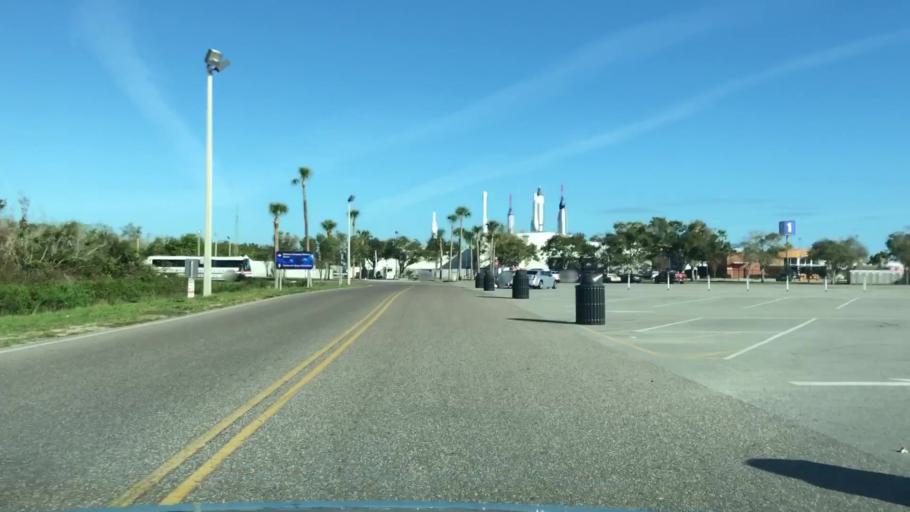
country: US
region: Florida
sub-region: Brevard County
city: Merritt Island
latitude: 28.5209
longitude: -80.6834
